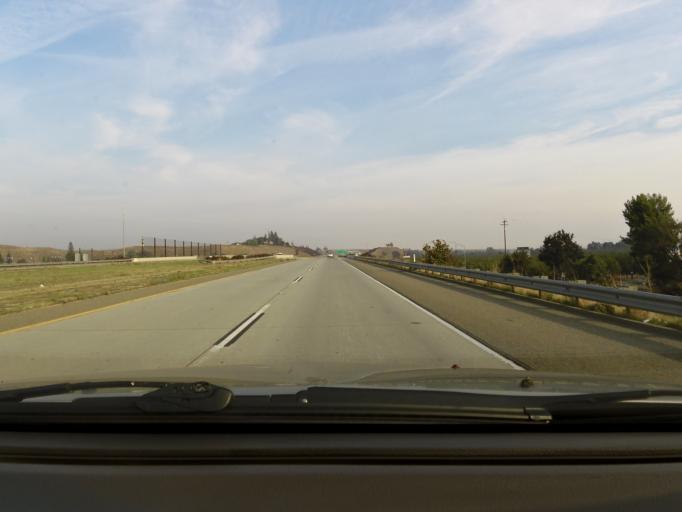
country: US
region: California
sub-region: Fresno County
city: Clovis
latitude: 36.8795
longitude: -119.7926
